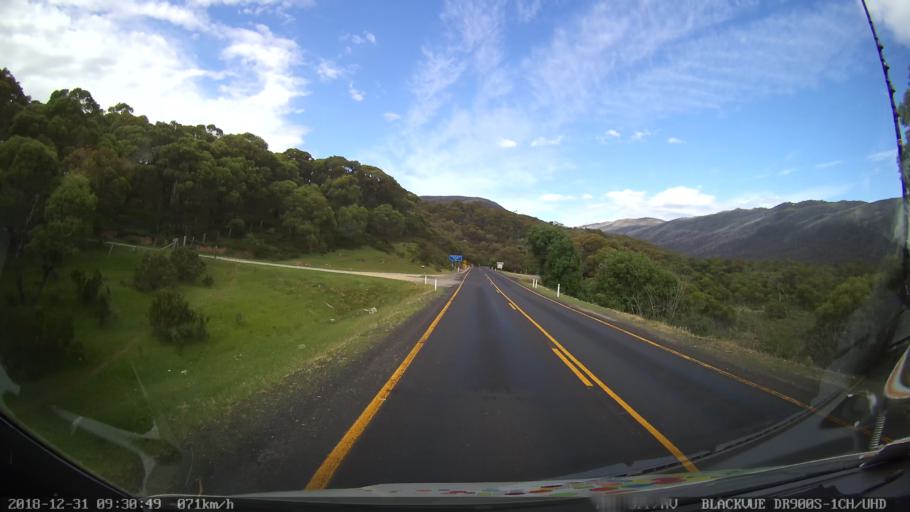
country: AU
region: New South Wales
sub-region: Snowy River
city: Jindabyne
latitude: -36.4500
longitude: 148.4499
